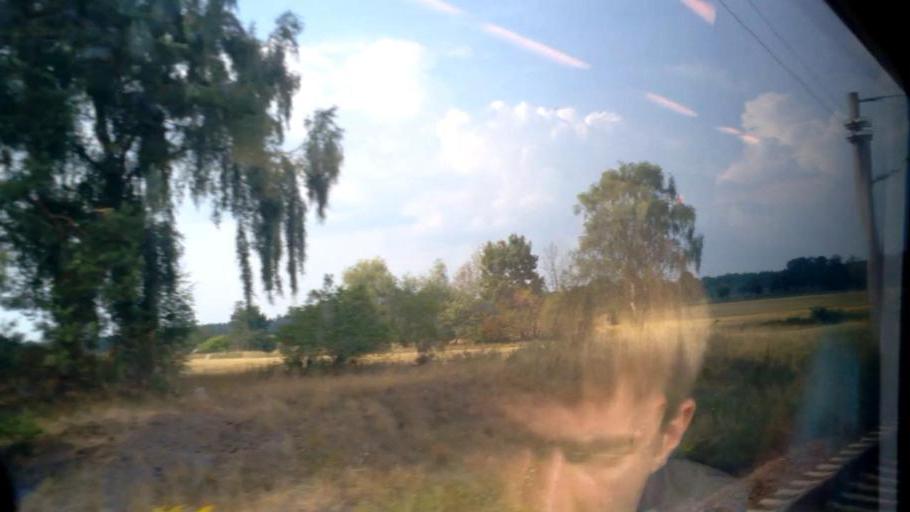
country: DE
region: Brandenburg
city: Ludwigsfelde
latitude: 52.3373
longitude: 13.2554
